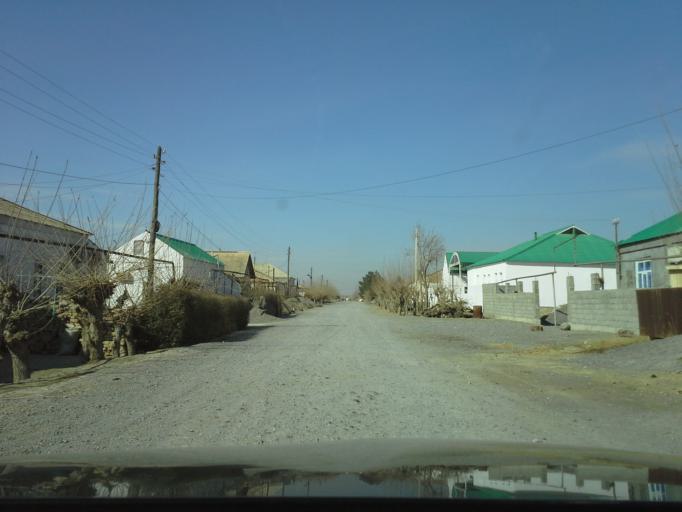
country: TM
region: Ahal
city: Abadan
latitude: 38.1224
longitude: 58.0000
